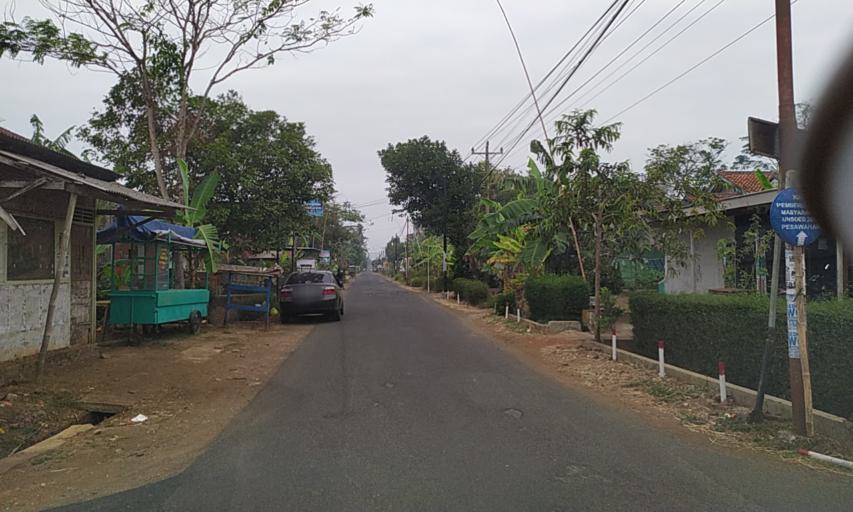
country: ID
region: Central Java
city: Kroya
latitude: -7.6711
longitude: 109.2841
